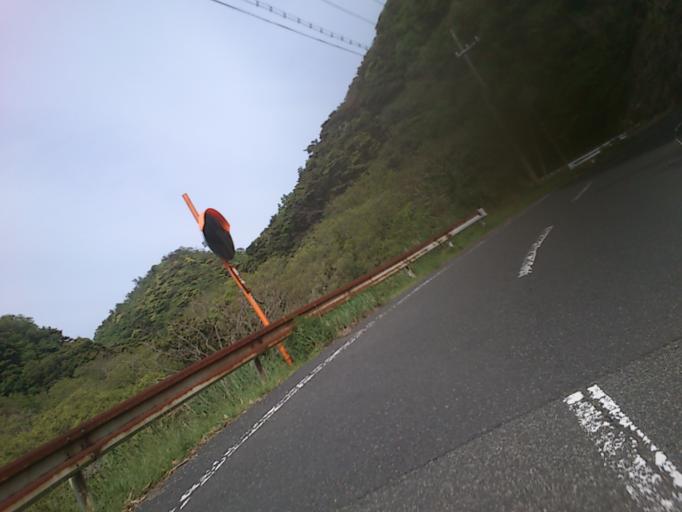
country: JP
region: Hyogo
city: Toyooka
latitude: 35.6764
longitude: 134.9737
